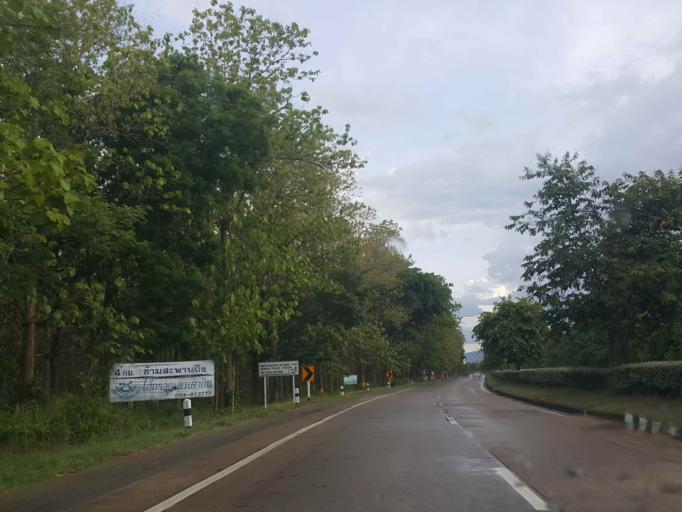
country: TH
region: Phrae
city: Sung Men
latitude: 17.9988
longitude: 100.1025
